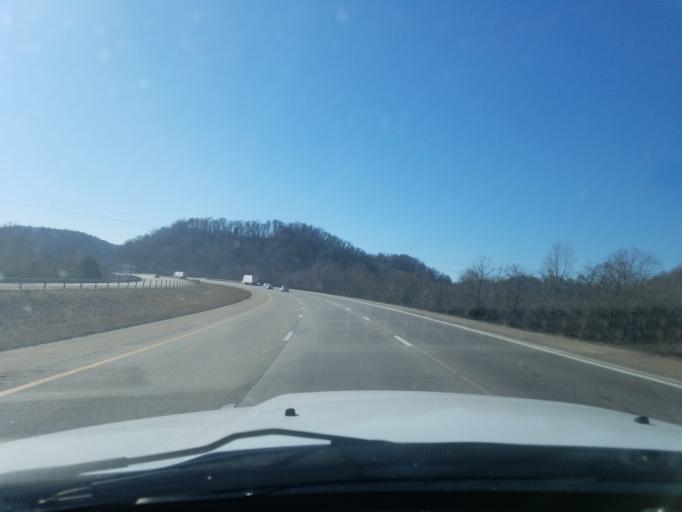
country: US
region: Kentucky
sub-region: Bullitt County
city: Lebanon Junction
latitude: 37.7877
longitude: -85.7701
